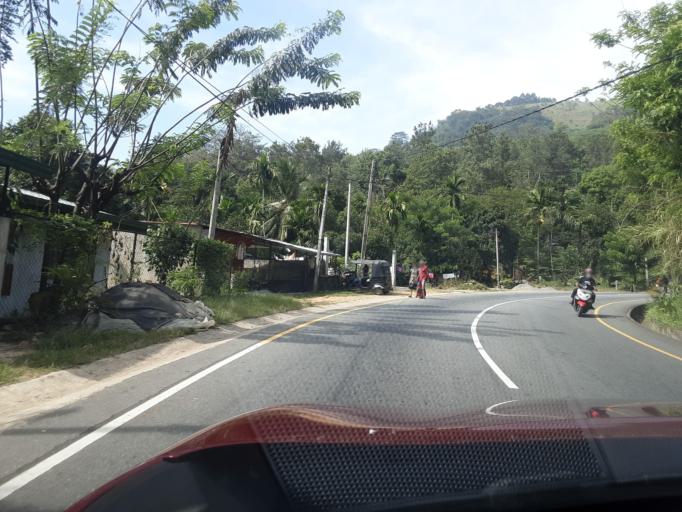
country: LK
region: Uva
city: Badulla
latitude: 6.9809
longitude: 81.0806
